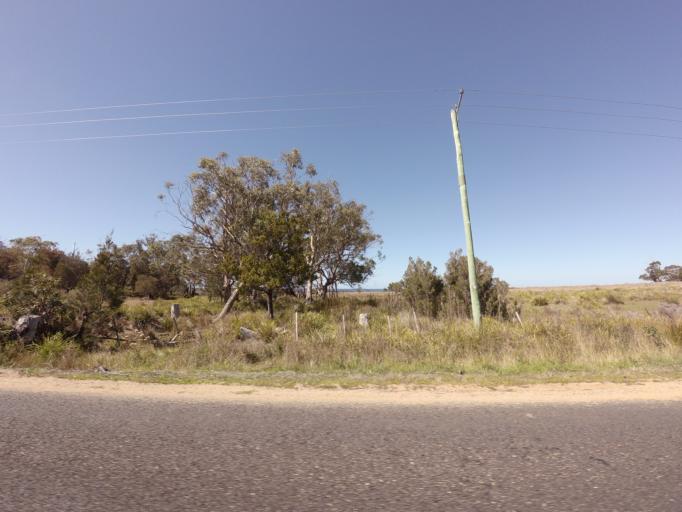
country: AU
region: Tasmania
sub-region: Break O'Day
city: St Helens
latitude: -41.6986
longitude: 148.2767
